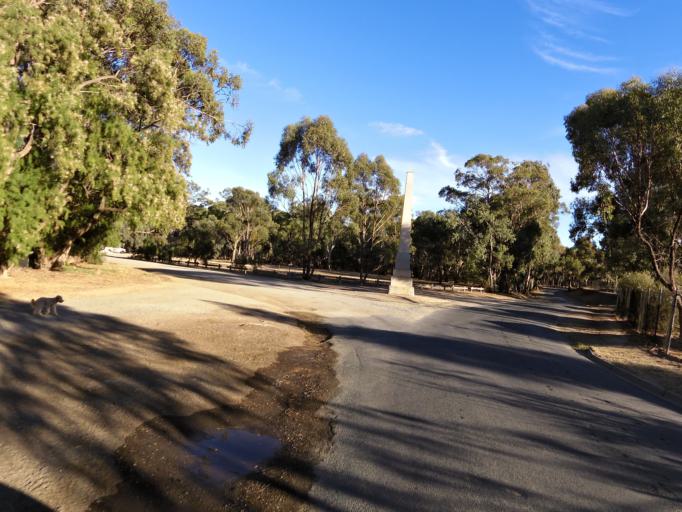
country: AU
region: New South Wales
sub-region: Murray Shire
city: Moama
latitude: -36.1157
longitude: 144.7415
